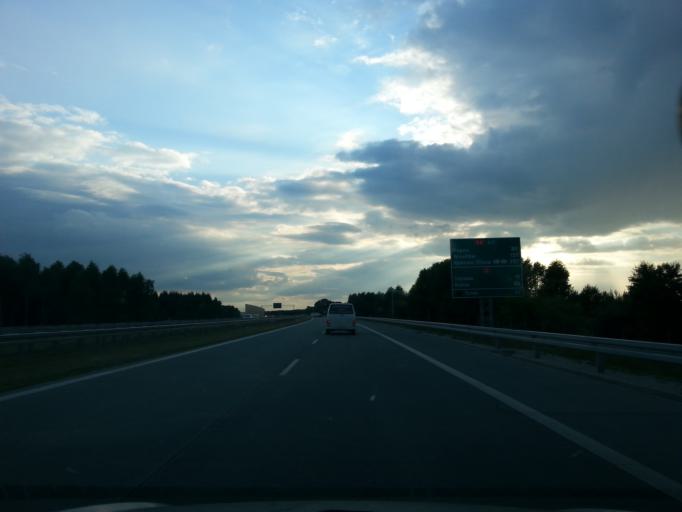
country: PL
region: Lodz Voivodeship
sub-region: Powiat zdunskowolski
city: Zapolice
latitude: 51.5986
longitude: 18.8641
